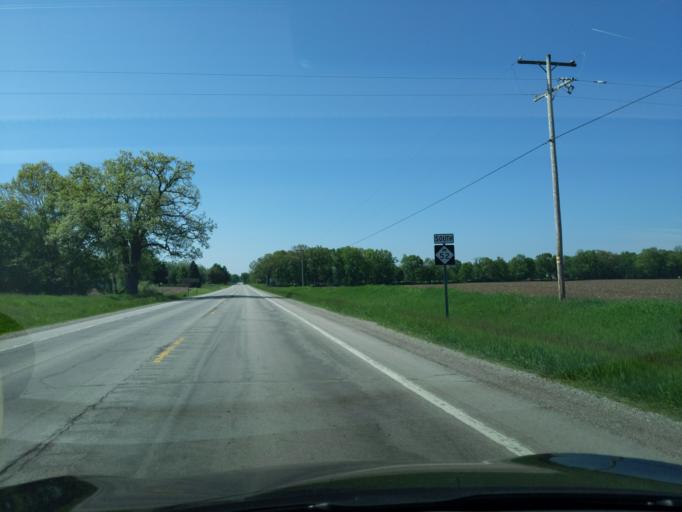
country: US
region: Michigan
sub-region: Ingham County
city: Stockbridge
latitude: 42.5010
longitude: -84.1902
